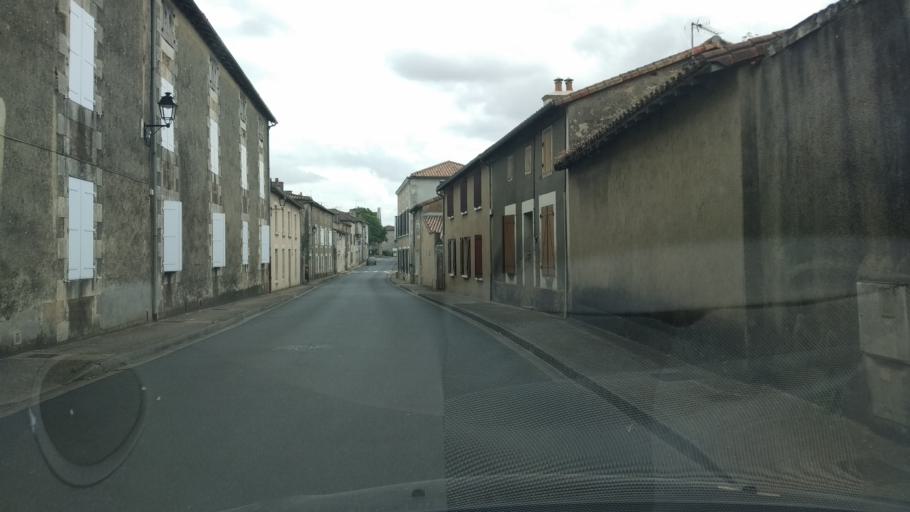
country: FR
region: Poitou-Charentes
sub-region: Departement de la Vienne
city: La Villedieu-du-Clain
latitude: 46.4576
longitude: 0.3670
